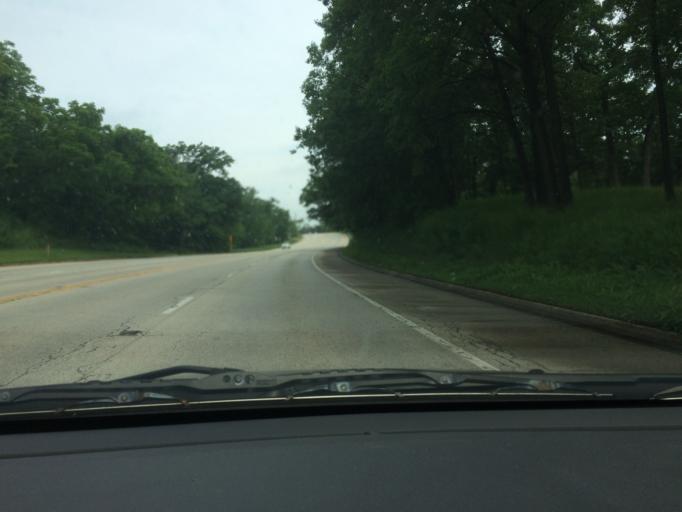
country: US
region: Illinois
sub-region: DuPage County
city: Wayne
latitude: 41.9443
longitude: -88.2008
